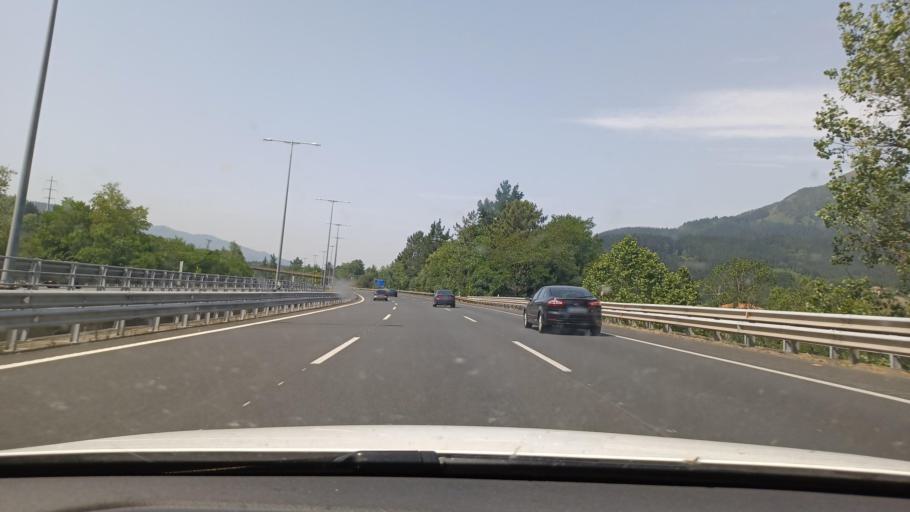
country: ES
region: Basque Country
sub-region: Bizkaia
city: Elexalde
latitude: 43.1734
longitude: -2.9140
